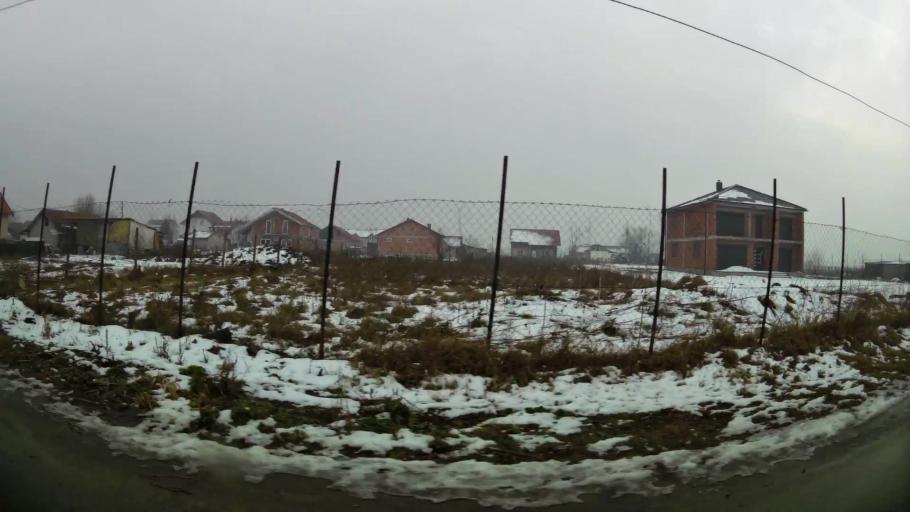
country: MK
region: Petrovec
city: Petrovec
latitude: 41.9347
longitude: 21.6086
